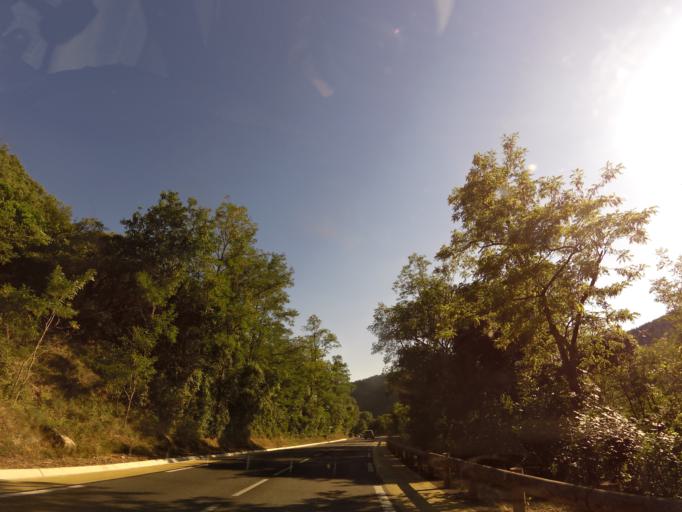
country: FR
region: Languedoc-Roussillon
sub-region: Departement de l'Herault
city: Ganges
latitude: 43.9544
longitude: 3.6868
